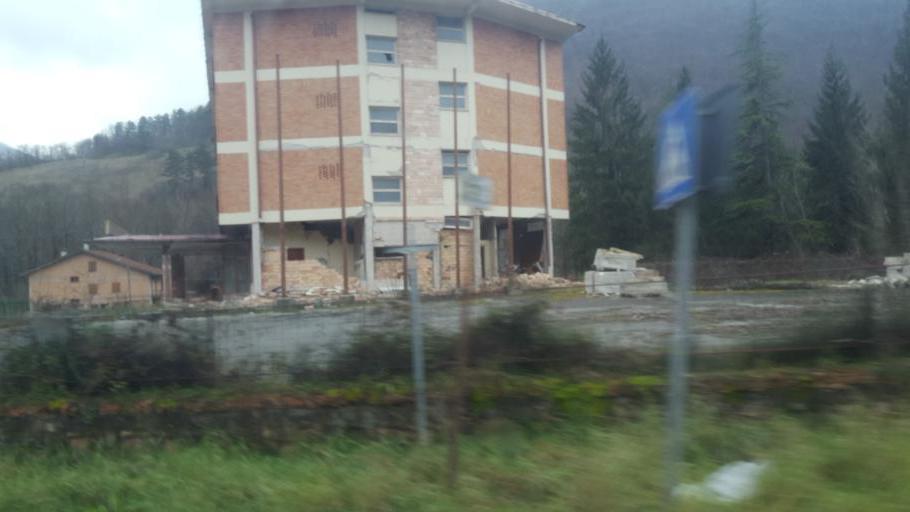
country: IT
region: The Marches
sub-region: Provincia di Macerata
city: Visso
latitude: 42.9332
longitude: 13.0831
